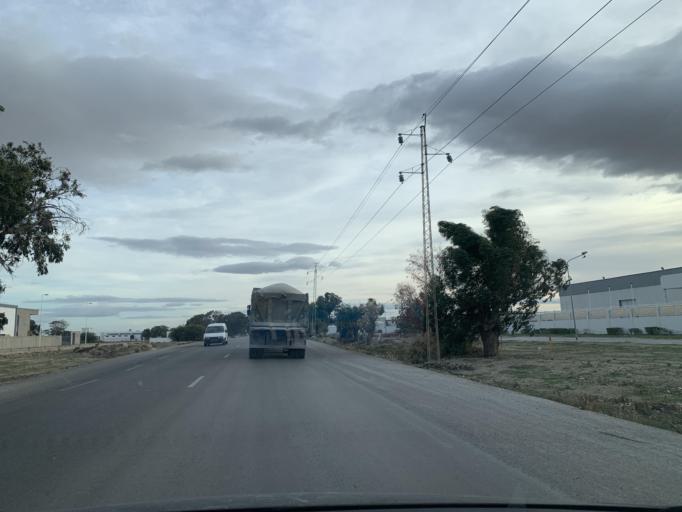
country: TN
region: Susah
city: Harqalah
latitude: 36.1085
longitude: 10.3866
